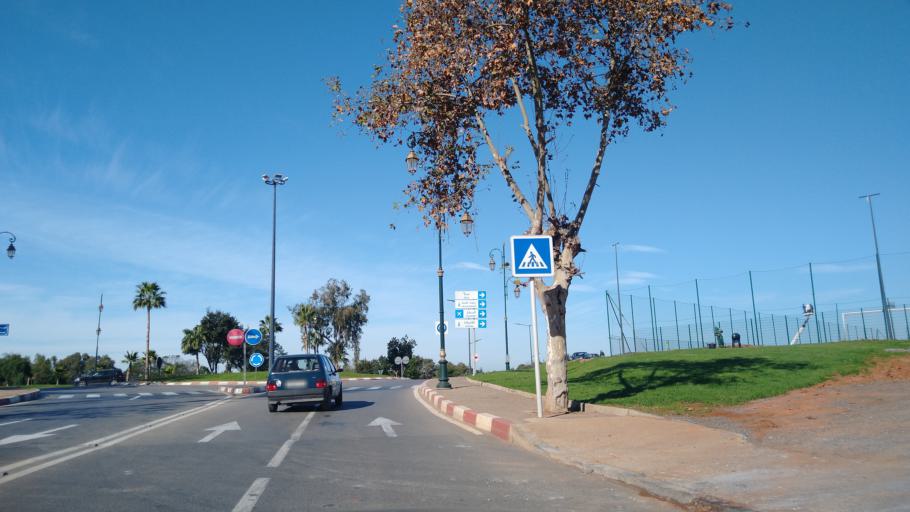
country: MA
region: Rabat-Sale-Zemmour-Zaer
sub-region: Rabat
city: Rabat
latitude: 33.9991
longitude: -6.8246
